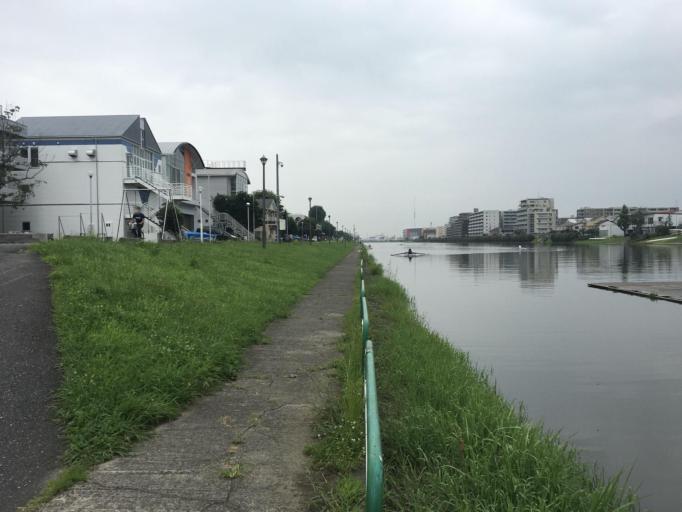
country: JP
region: Saitama
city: Shimotoda
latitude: 35.8018
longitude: 139.6806
